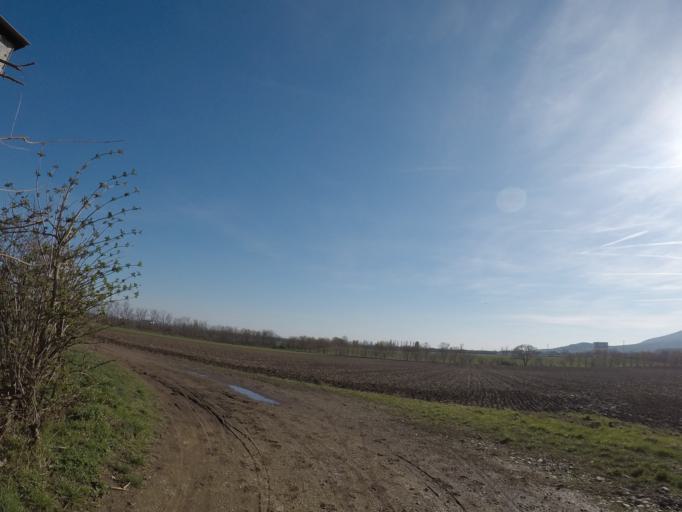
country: AT
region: Lower Austria
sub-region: Politischer Bezirk Modling
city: Vosendorf
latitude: 48.1041
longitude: 16.3312
